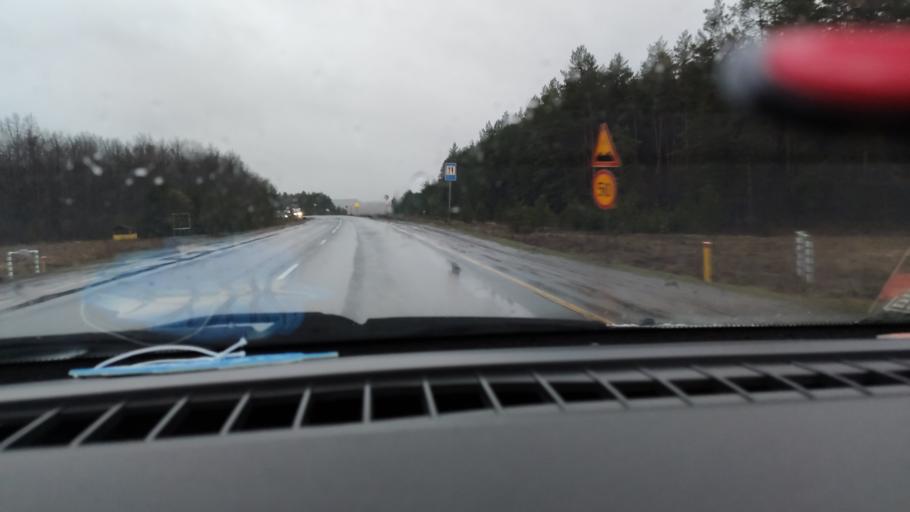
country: RU
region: Tatarstan
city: Mendeleyevsk
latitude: 55.9454
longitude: 52.2957
